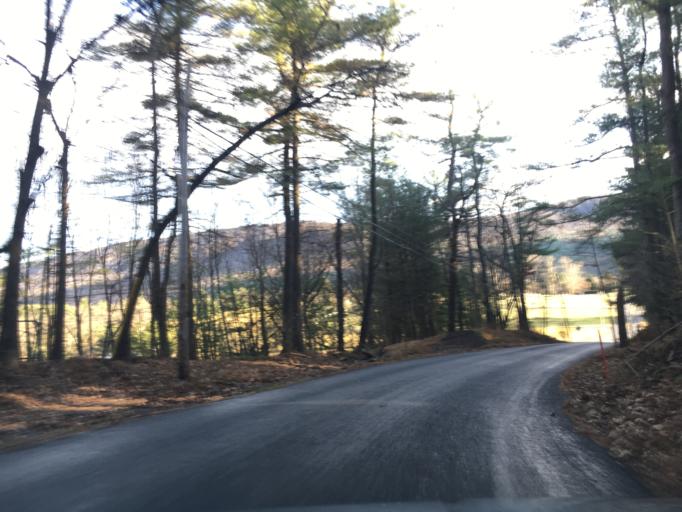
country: US
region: Pennsylvania
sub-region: Carbon County
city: Lehighton
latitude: 40.7899
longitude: -75.7163
